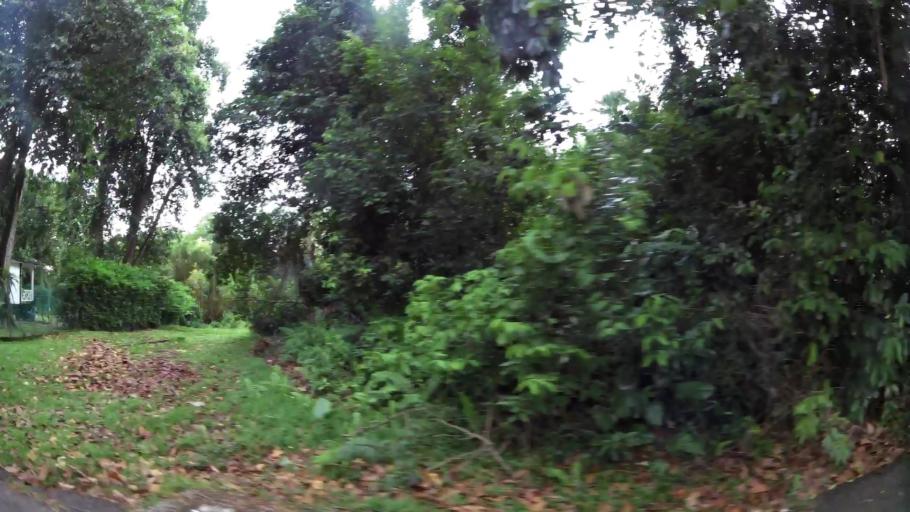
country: SG
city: Singapore
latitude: 1.2849
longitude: 103.7961
